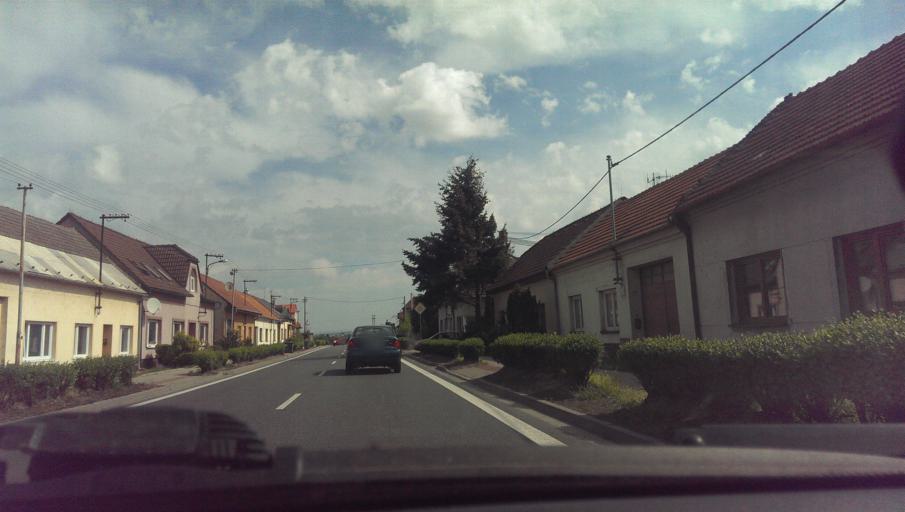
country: CZ
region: Zlin
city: Babice
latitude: 49.1092
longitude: 17.4659
